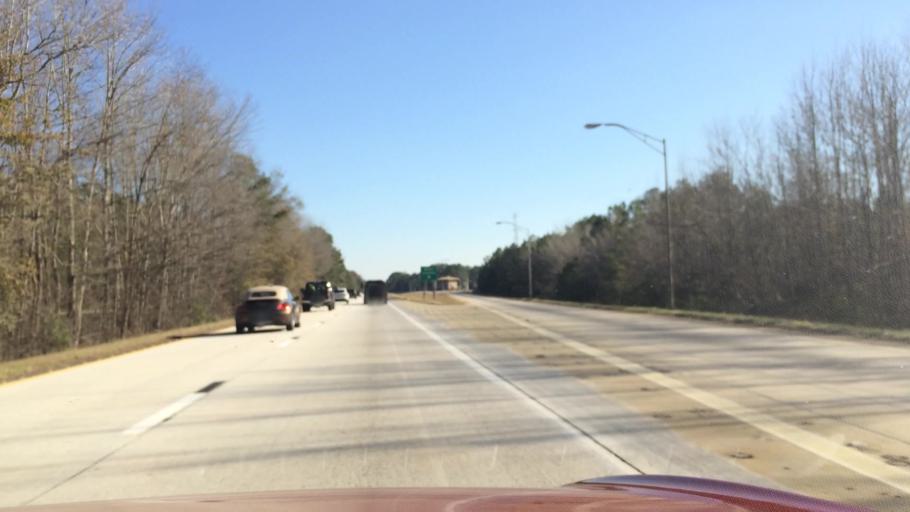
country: US
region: South Carolina
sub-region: Orangeburg County
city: Holly Hill
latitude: 33.2727
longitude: -80.4917
